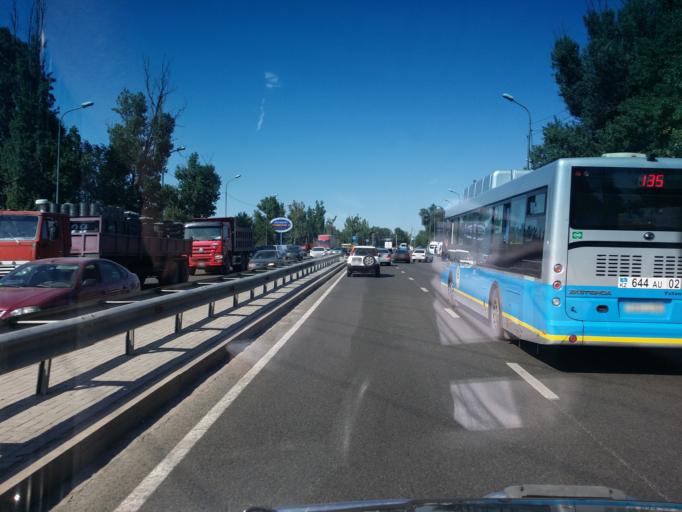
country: KZ
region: Almaty Oblysy
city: Burunday
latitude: 43.3219
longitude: 76.9056
